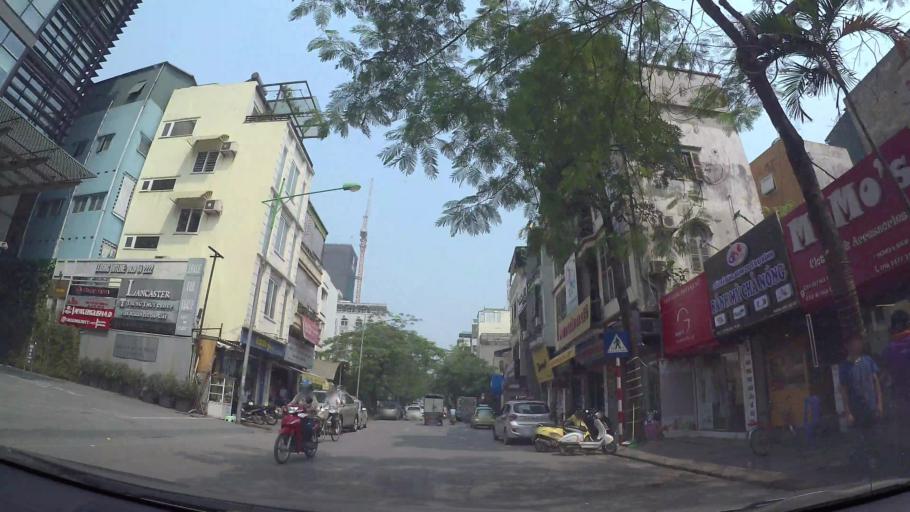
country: VN
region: Ha Noi
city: Dong Da
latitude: 21.0290
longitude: 105.8237
